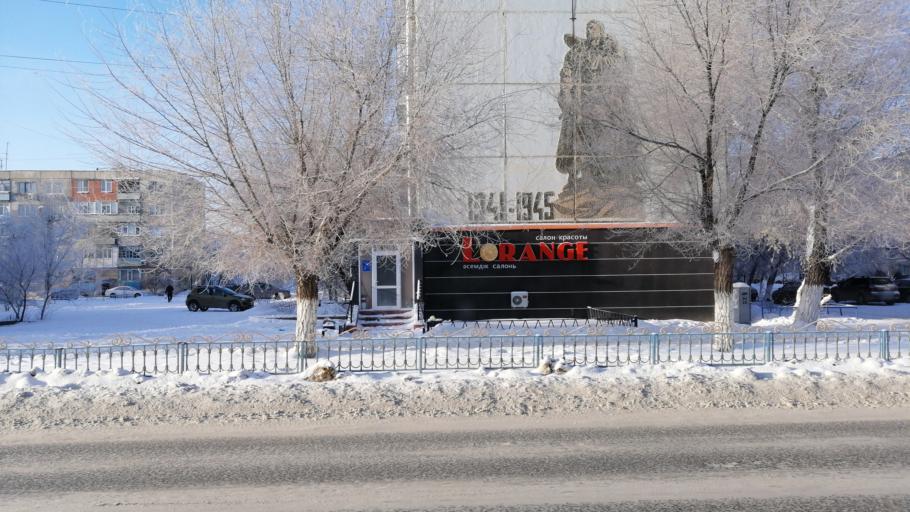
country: KZ
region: Aqtoebe
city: Aqtobe
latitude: 50.3042
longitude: 57.1518
